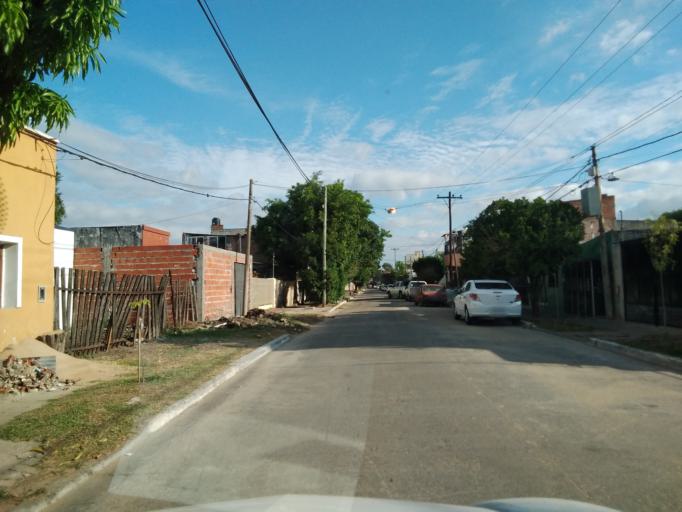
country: AR
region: Corrientes
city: Corrientes
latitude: -27.4636
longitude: -58.8193
